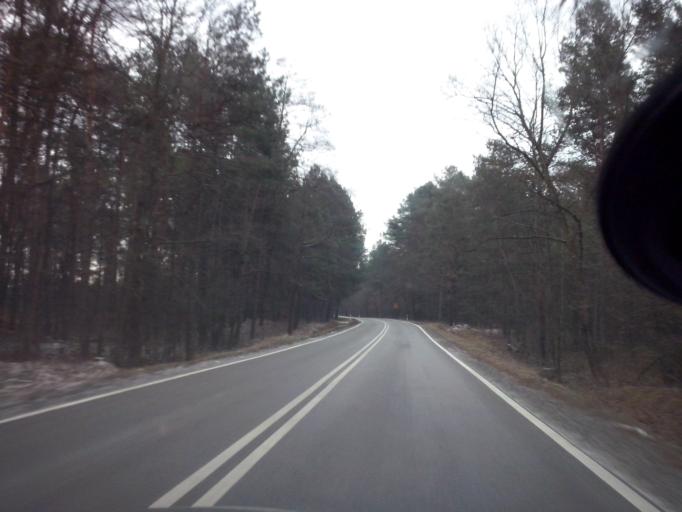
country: PL
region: Lublin Voivodeship
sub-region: Powiat bilgorajski
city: Biszcza
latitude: 50.4993
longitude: 22.6098
